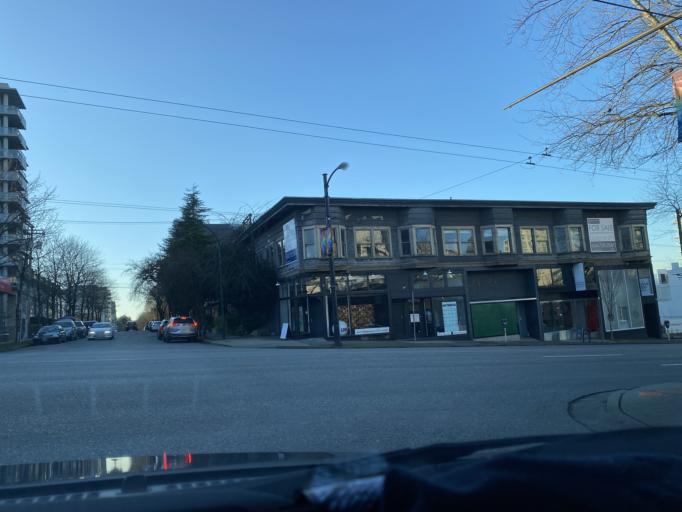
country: CA
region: British Columbia
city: West End
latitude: 49.2645
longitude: -123.1383
